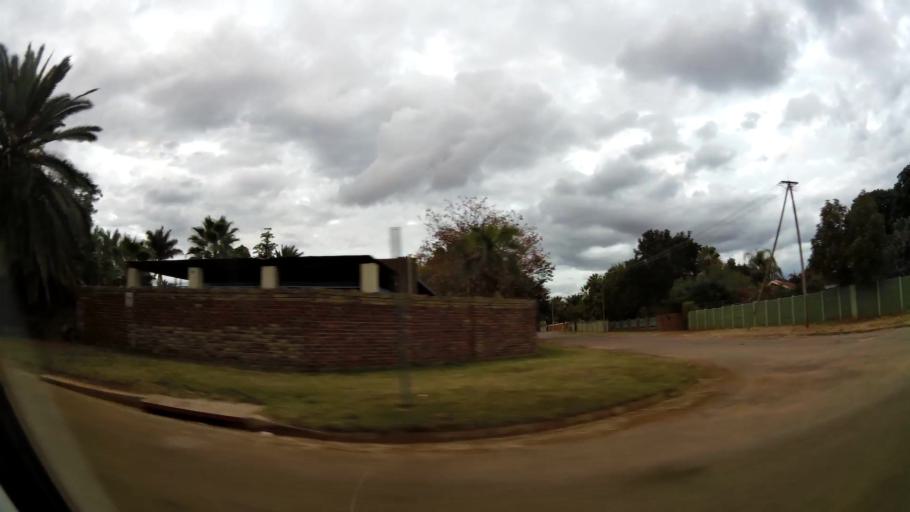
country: ZA
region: Limpopo
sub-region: Waterberg District Municipality
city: Mokopane
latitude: -24.1874
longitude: 28.9908
